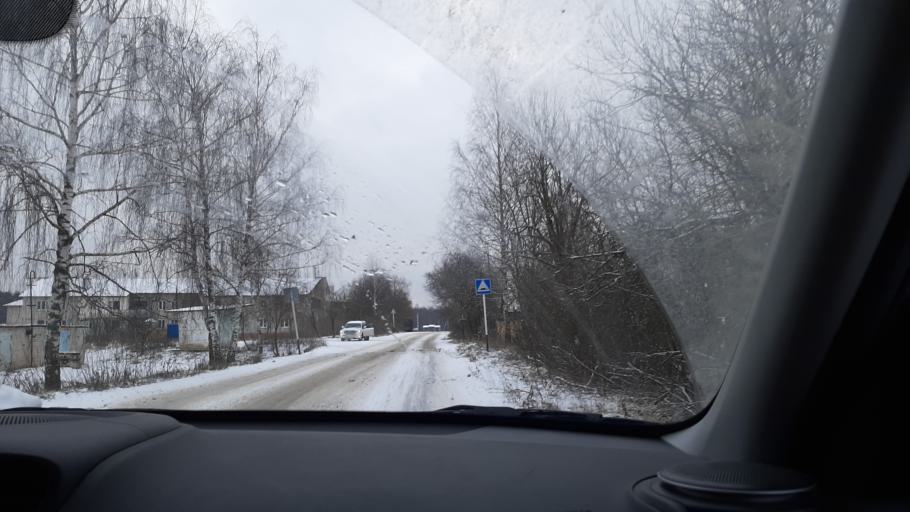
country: RU
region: Ivanovo
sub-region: Gorod Ivanovo
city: Ivanovo
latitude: 56.9273
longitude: 40.9821
